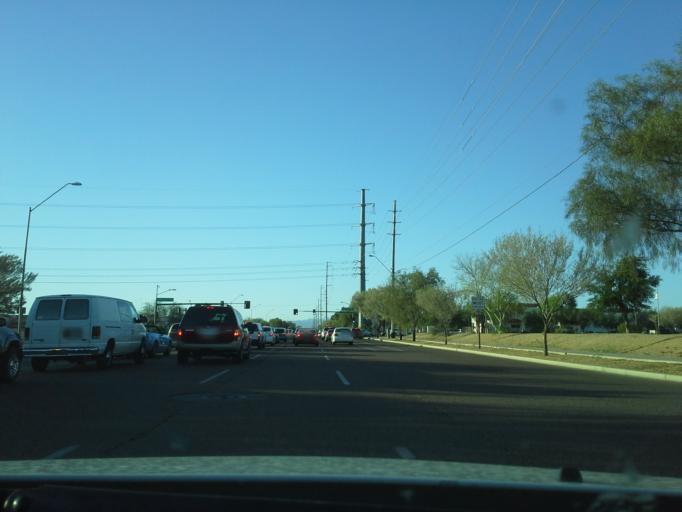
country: US
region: Arizona
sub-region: Maricopa County
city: Paradise Valley
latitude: 33.6538
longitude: -112.0135
